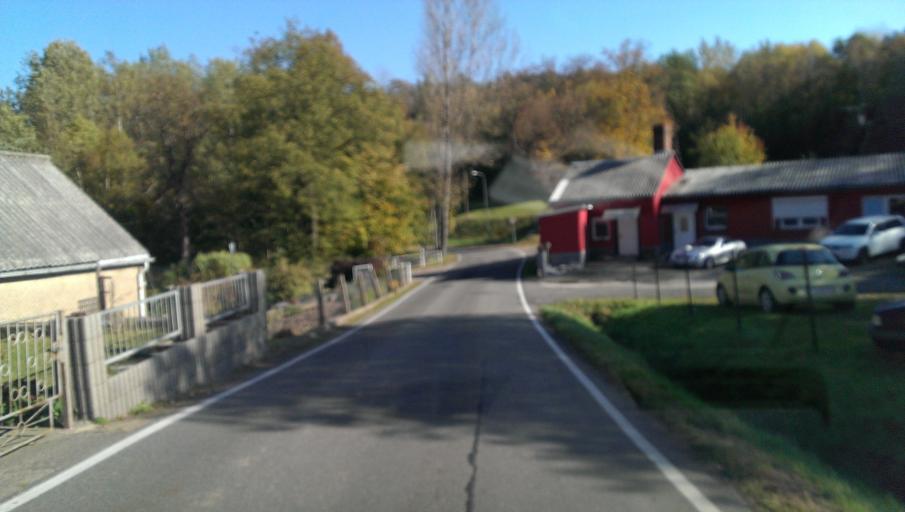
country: DE
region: Saxony
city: Kriebstein
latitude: 51.0626
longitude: 13.0085
